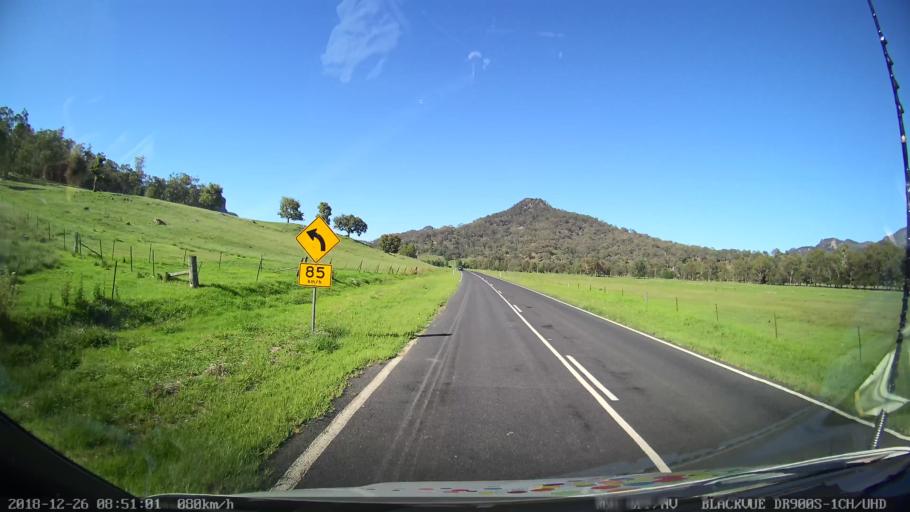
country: AU
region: New South Wales
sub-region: Mid-Western Regional
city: Kandos
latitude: -32.5815
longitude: 150.0907
